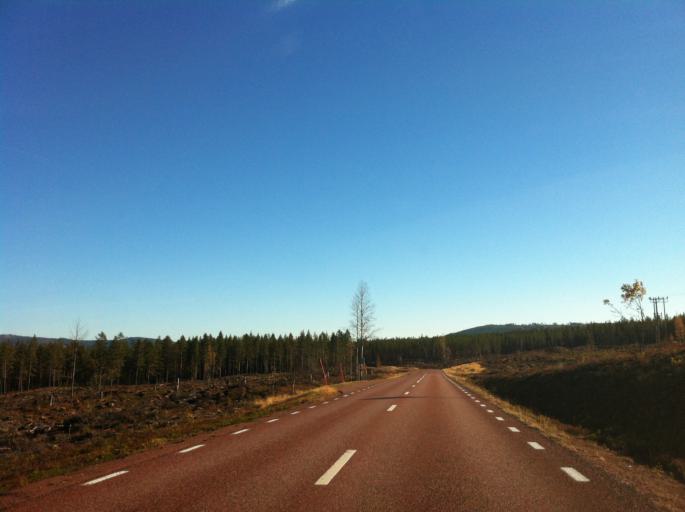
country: SE
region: Dalarna
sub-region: Alvdalens Kommun
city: AElvdalen
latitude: 61.3270
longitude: 13.6062
